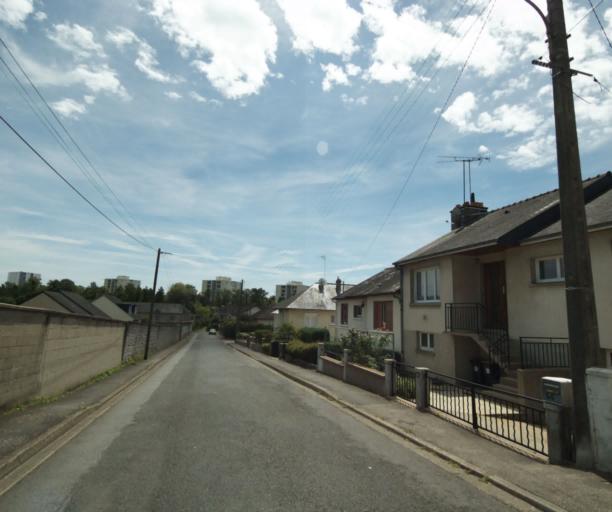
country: FR
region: Pays de la Loire
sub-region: Departement de la Mayenne
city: Laval
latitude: 48.0667
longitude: -0.7542
